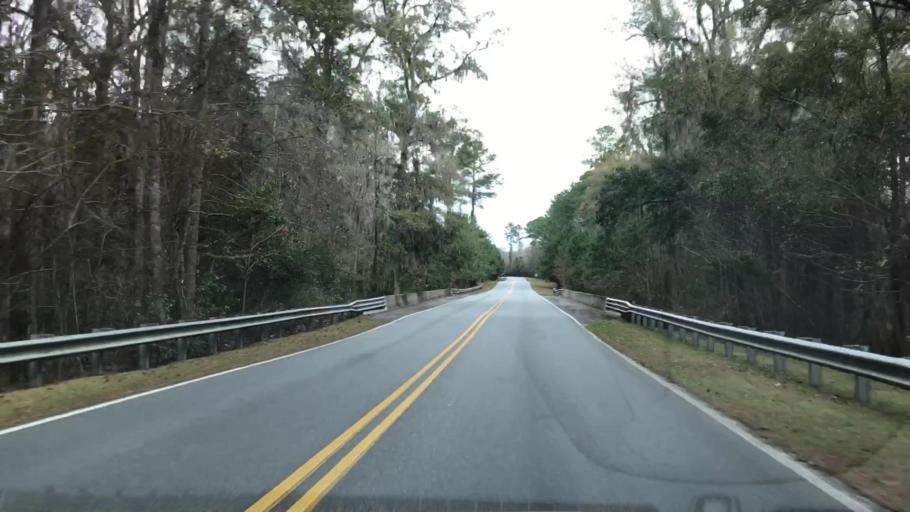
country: US
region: South Carolina
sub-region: Beaufort County
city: Bluffton
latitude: 32.2804
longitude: -80.9275
